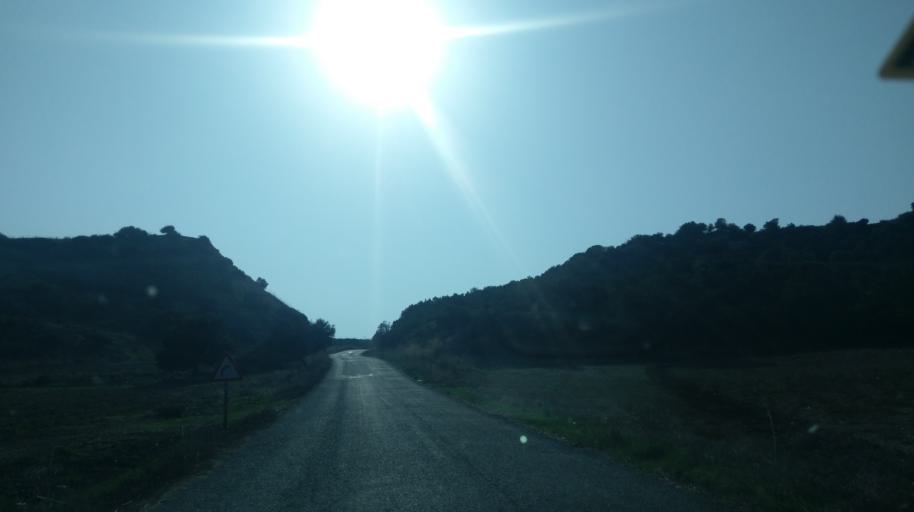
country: CY
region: Ammochostos
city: Rizokarpaso
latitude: 35.5280
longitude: 34.3275
